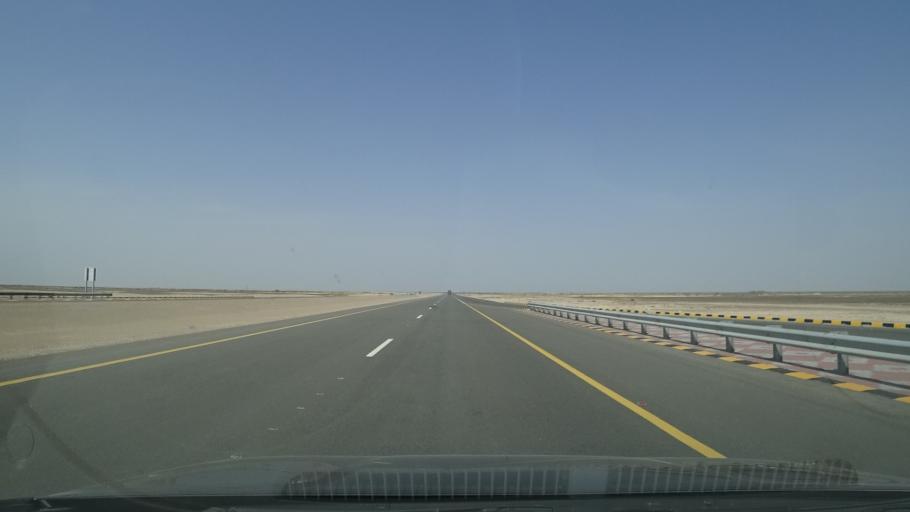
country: OM
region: Muhafazat ad Dakhiliyah
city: Adam
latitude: 21.8147
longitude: 57.3591
